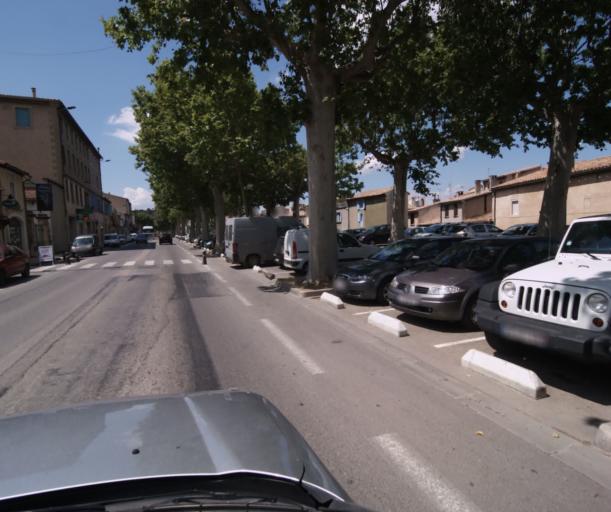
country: FR
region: Languedoc-Roussillon
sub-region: Departement de l'Aude
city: Limoux
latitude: 43.0517
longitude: 2.2168
